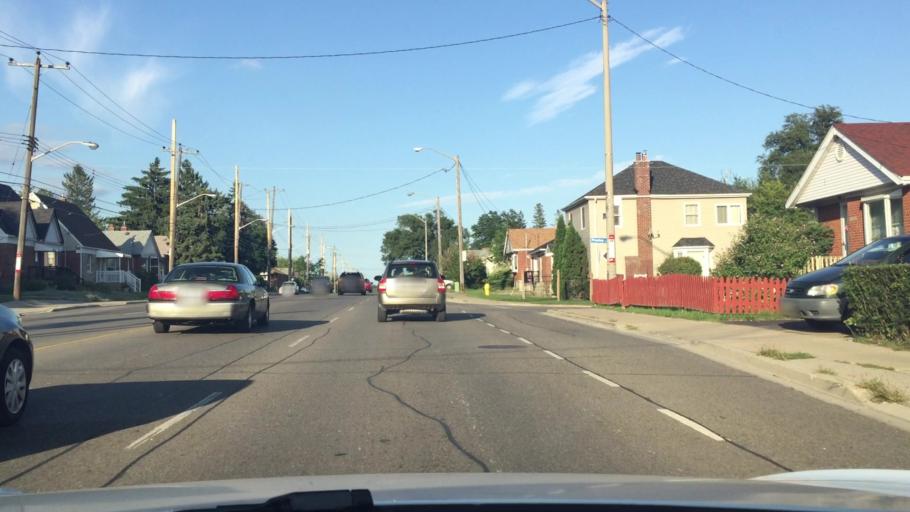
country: CA
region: Ontario
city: Scarborough
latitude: 43.7103
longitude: -79.2889
